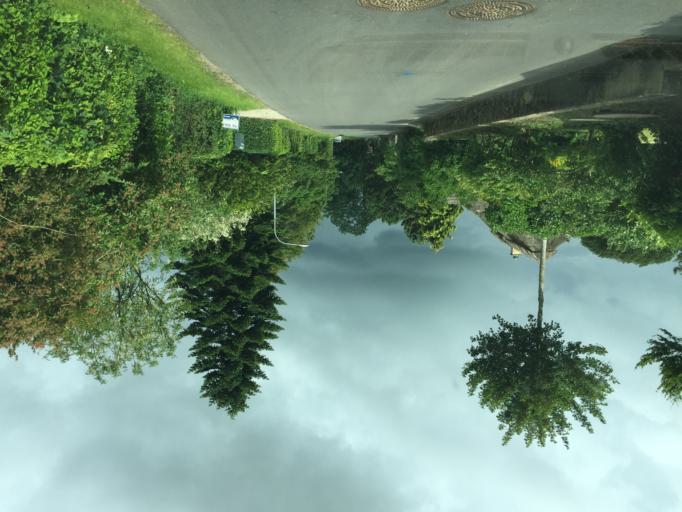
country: DK
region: South Denmark
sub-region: Faaborg-Midtfyn Kommune
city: Arslev
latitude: 55.2973
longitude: 10.4596
